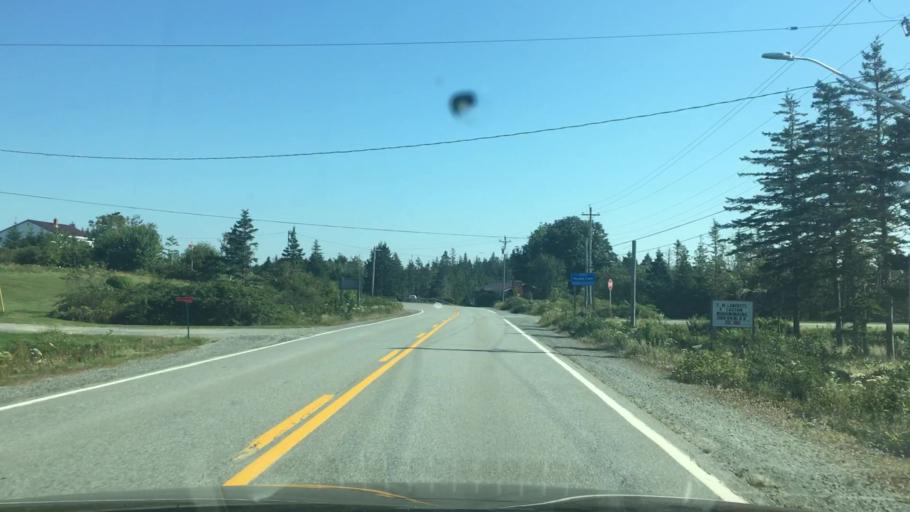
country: CA
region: Nova Scotia
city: Cole Harbour
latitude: 44.7813
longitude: -62.7710
